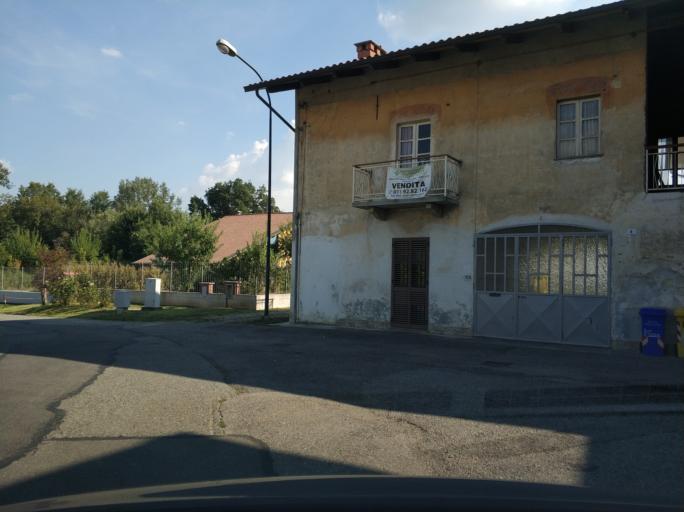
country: IT
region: Piedmont
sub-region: Provincia di Torino
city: Grosso
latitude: 45.2598
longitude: 7.5705
